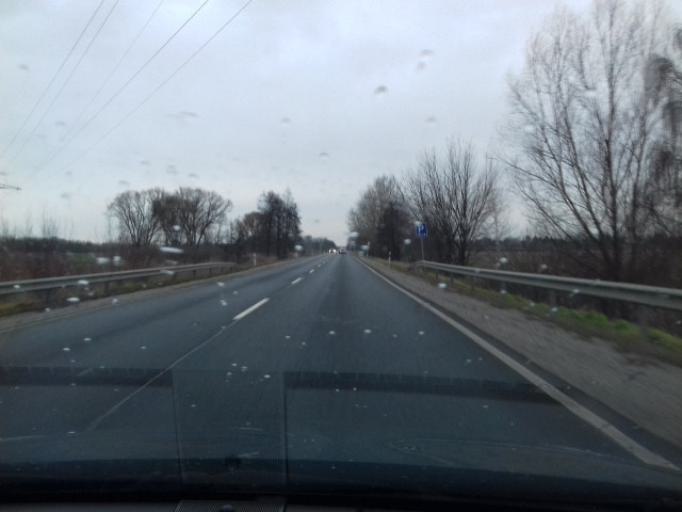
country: HU
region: Szabolcs-Szatmar-Bereg
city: Ujfeherto
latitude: 47.8734
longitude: 21.7056
